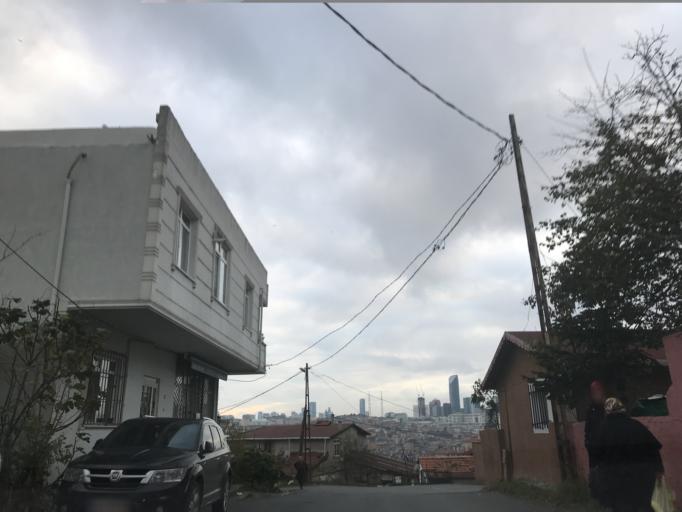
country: TR
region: Istanbul
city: Sisli
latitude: 41.1274
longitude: 29.0432
